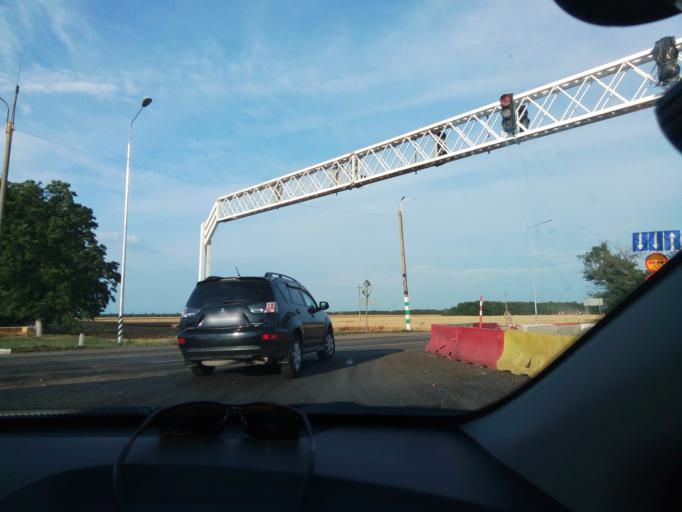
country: RU
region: Krasnodarskiy
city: Zavetnyy
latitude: 44.9495
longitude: 41.0871
